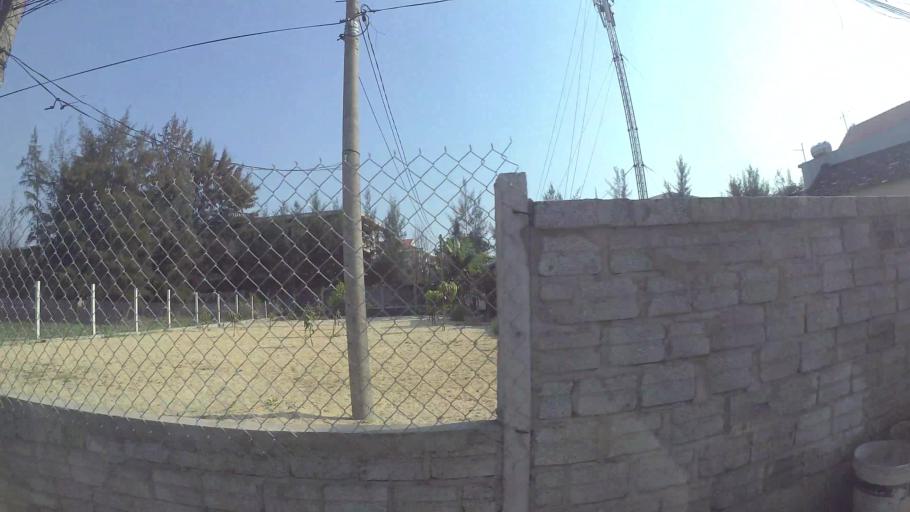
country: VN
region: Quang Nam
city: Quang Nam
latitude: 15.9469
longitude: 108.2557
